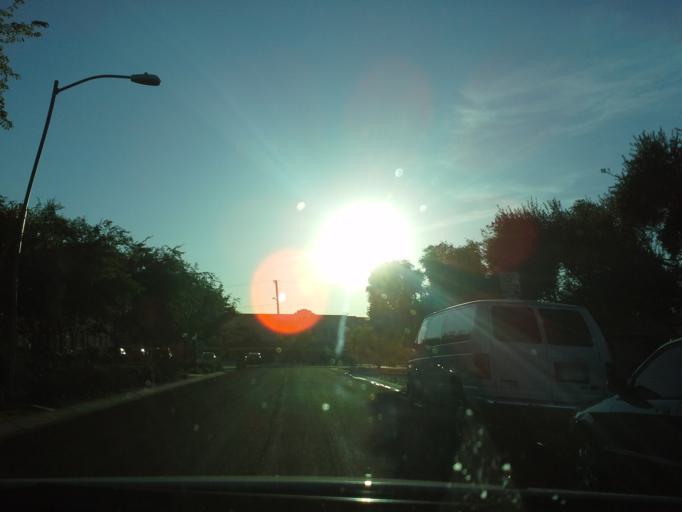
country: US
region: Arizona
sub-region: Maricopa County
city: Phoenix
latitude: 33.5060
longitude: -112.0685
